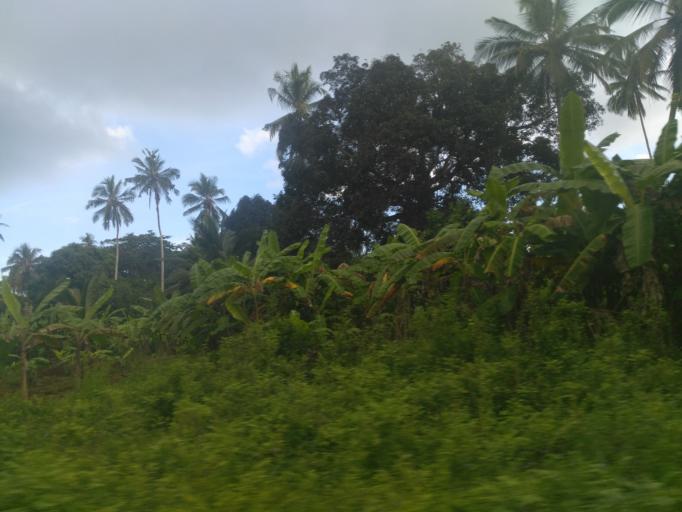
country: TZ
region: Zanzibar Central/South
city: Koani
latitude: -6.1059
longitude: 39.2883
